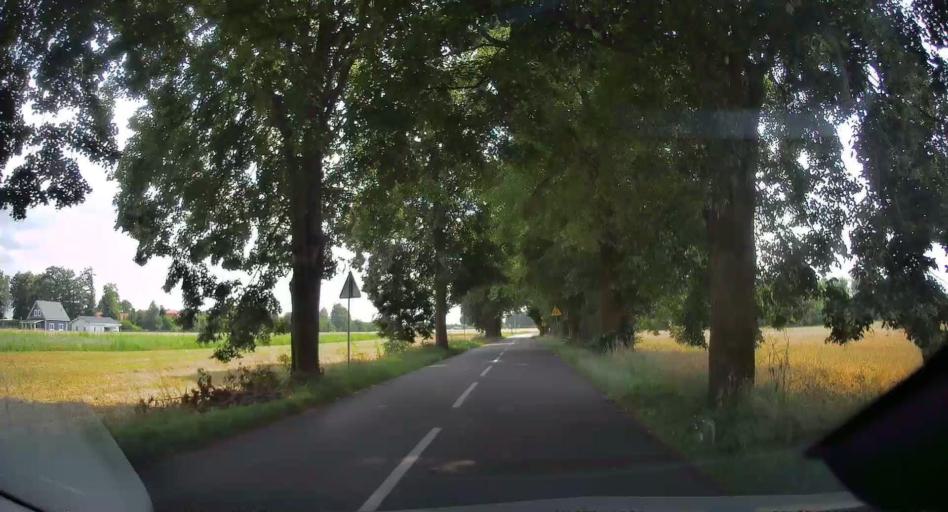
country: PL
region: Lodz Voivodeship
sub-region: Powiat tomaszowski
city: Lubochnia
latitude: 51.5692
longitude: 20.1034
